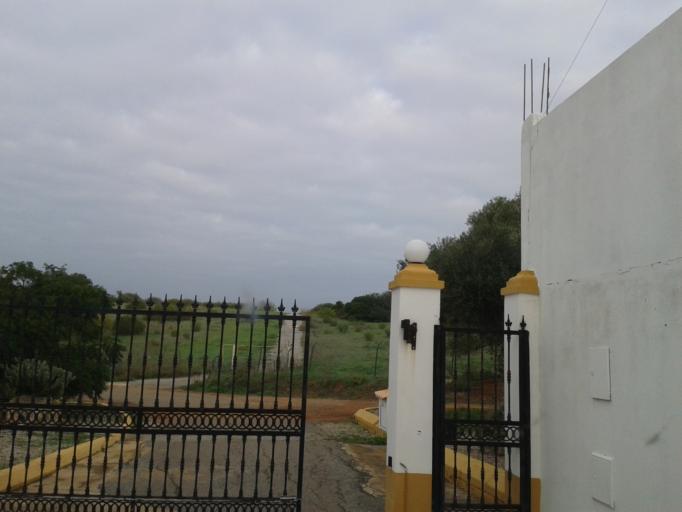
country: PT
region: Faro
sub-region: Vila Real de Santo Antonio
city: Monte Gordo
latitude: 37.1991
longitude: -7.4697
